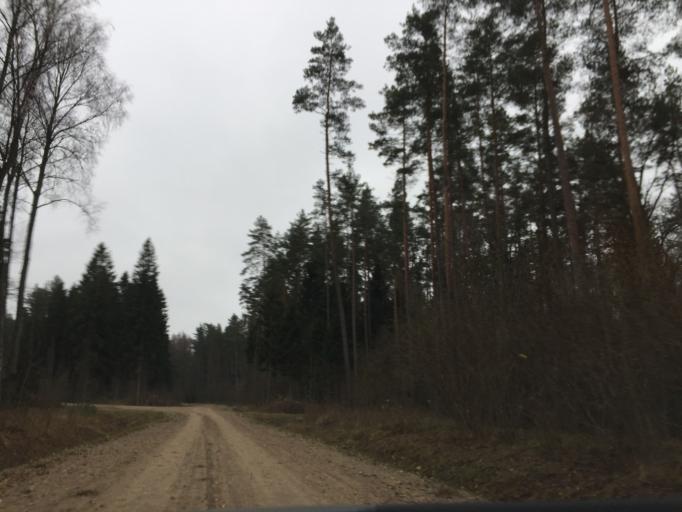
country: LV
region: Limbazu Rajons
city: Limbazi
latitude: 57.4639
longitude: 24.7564
